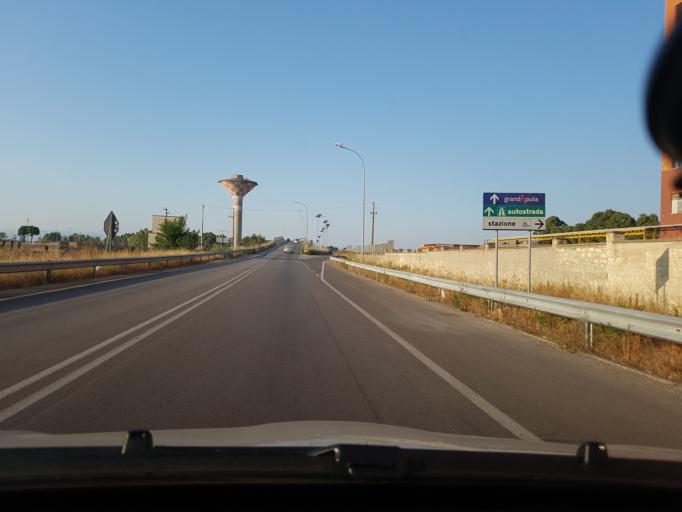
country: IT
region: Apulia
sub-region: Provincia di Foggia
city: Carapelle
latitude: 41.4035
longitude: 15.6508
